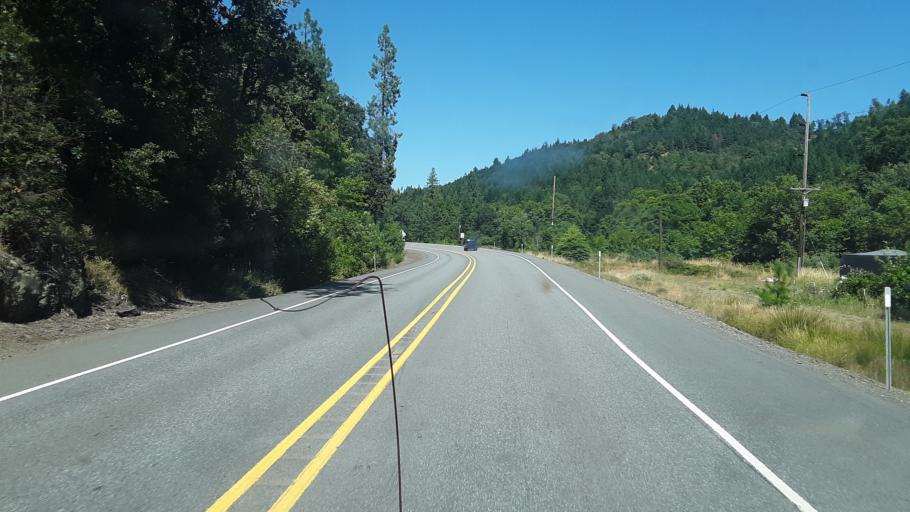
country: US
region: Oregon
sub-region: Josephine County
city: Redwood
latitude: 42.3641
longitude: -123.5122
